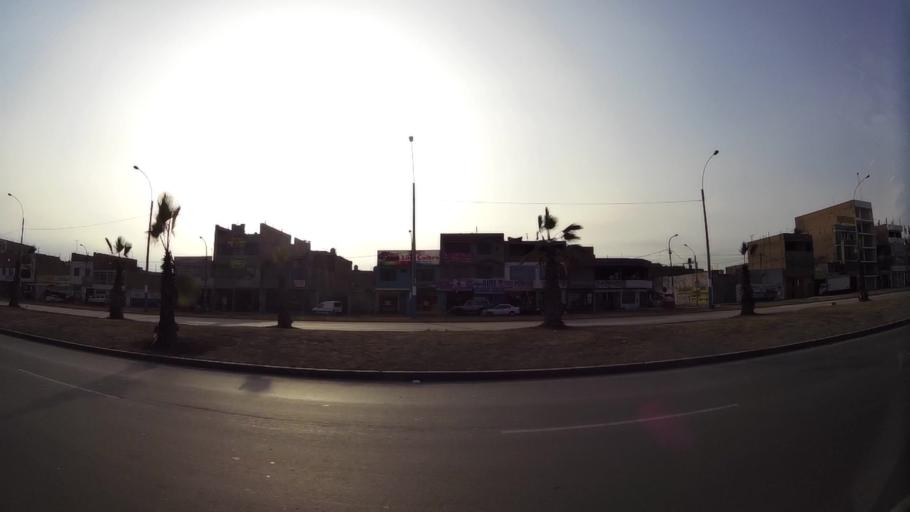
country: PE
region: Lima
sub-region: Lima
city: Independencia
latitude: -11.9789
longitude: -77.0942
